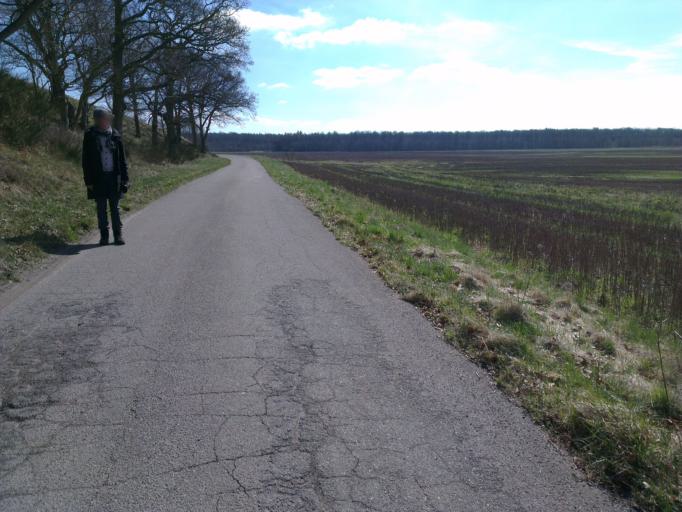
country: DK
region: Capital Region
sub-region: Frederikssund Kommune
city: Jaegerspris
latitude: 55.8940
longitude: 11.9870
